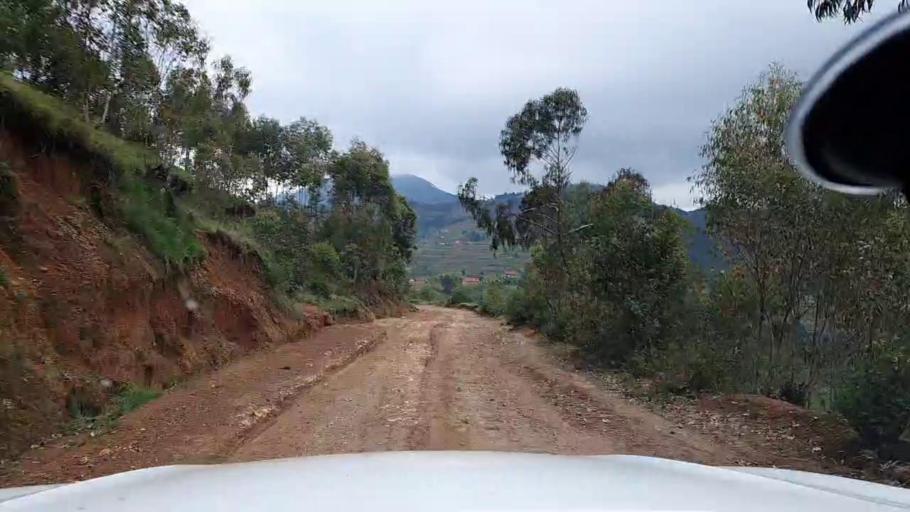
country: RW
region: Western Province
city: Kibuye
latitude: -2.0835
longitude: 29.5074
